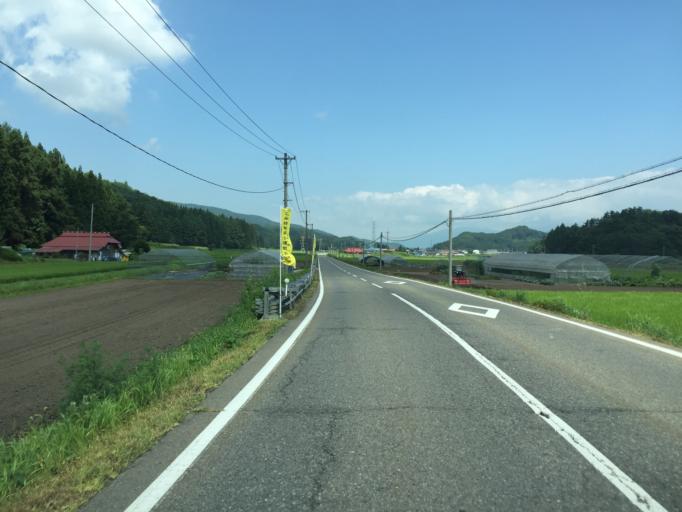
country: JP
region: Fukushima
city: Inawashiro
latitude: 37.4365
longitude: 140.0221
